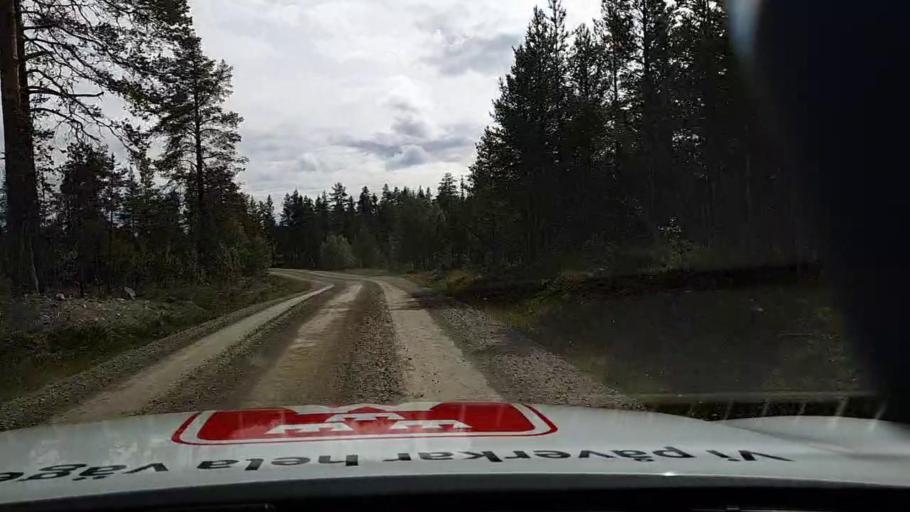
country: SE
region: Jaemtland
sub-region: Are Kommun
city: Jarpen
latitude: 62.5168
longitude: 13.4880
